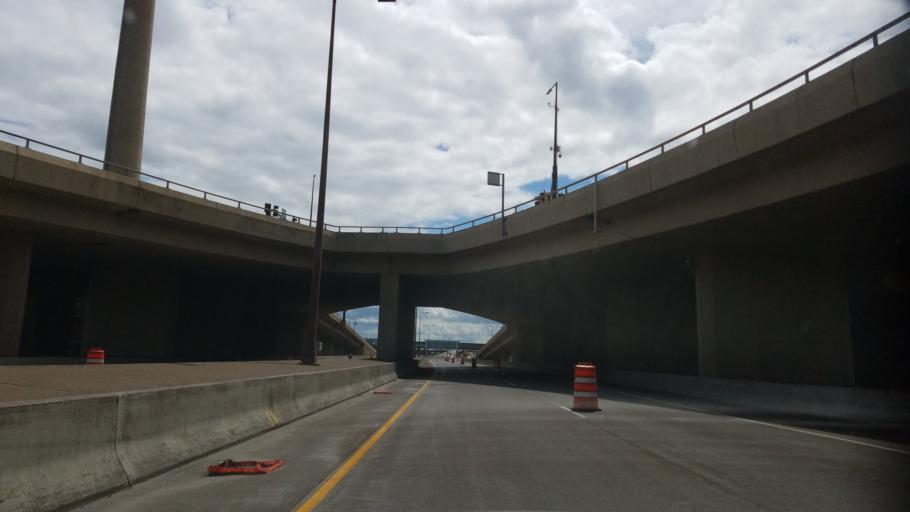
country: US
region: Minnesota
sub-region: Saint Louis County
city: Duluth
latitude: 46.7871
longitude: -92.0964
